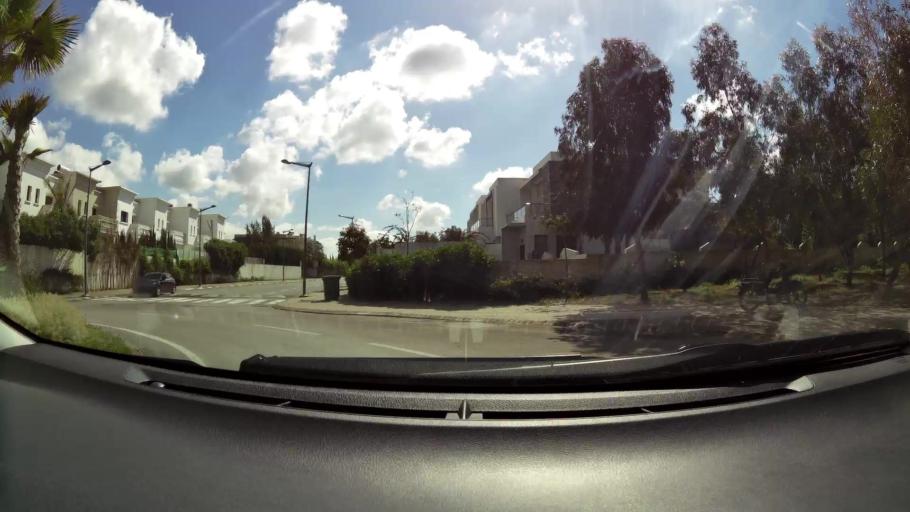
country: MA
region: Grand Casablanca
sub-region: Nouaceur
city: Bouskoura
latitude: 33.4717
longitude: -7.6008
